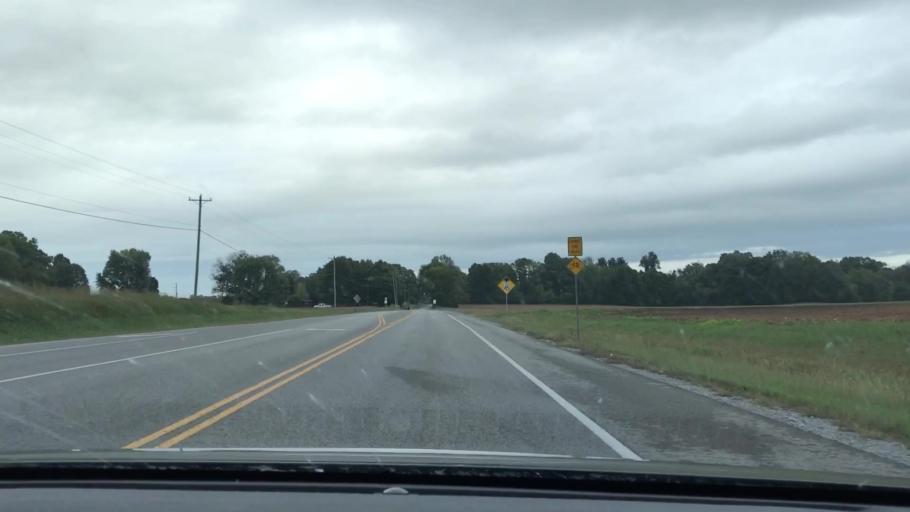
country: US
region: Kentucky
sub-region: Christian County
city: Hopkinsville
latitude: 36.8347
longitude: -87.5287
